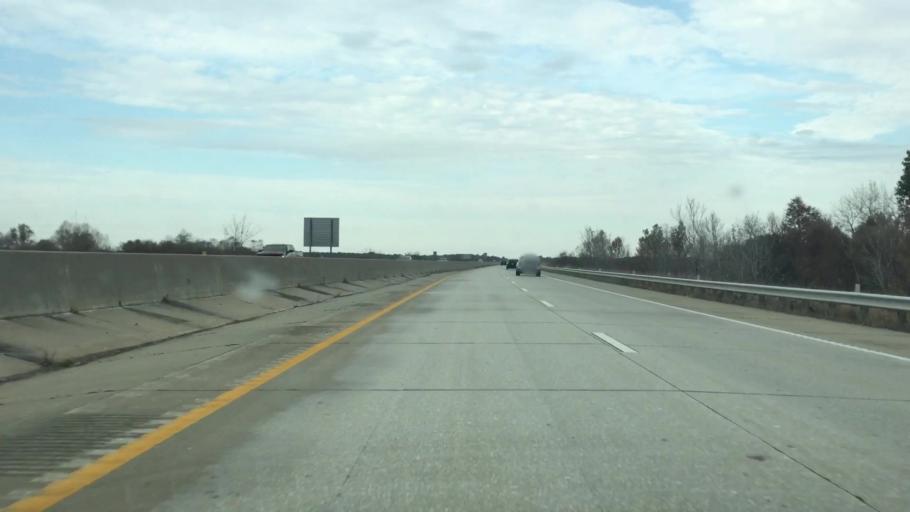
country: US
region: Missouri
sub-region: Henry County
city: Clinton
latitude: 38.2678
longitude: -93.7600
